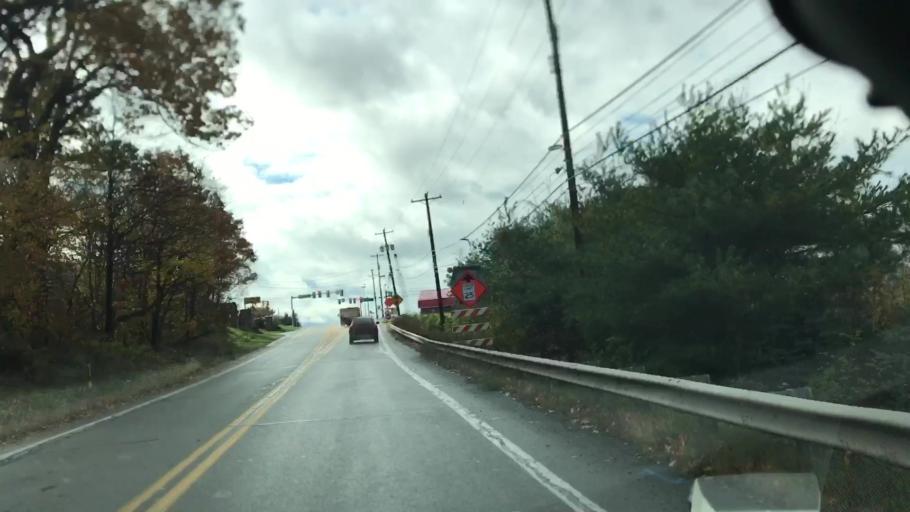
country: US
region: Pennsylvania
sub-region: Allegheny County
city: Carnot-Moon
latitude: 40.5172
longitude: -80.2676
